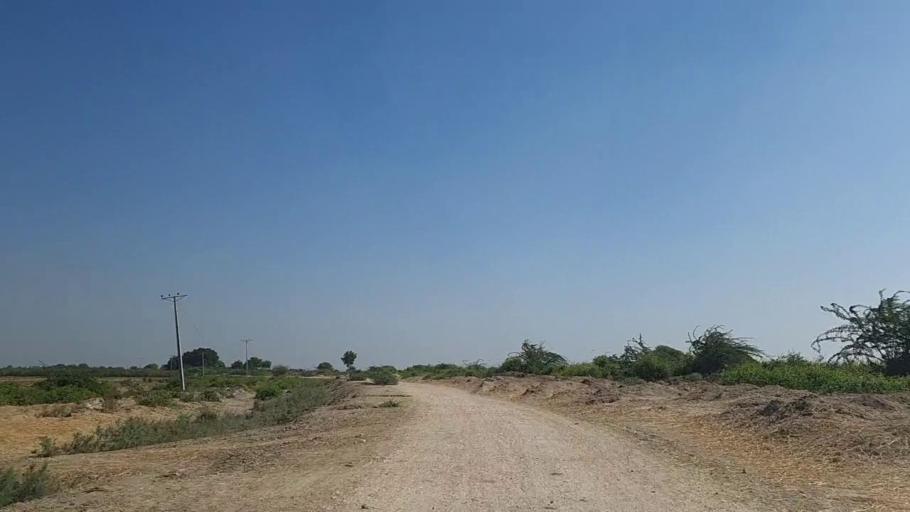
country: PK
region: Sindh
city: Daro Mehar
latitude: 24.7164
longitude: 68.1649
